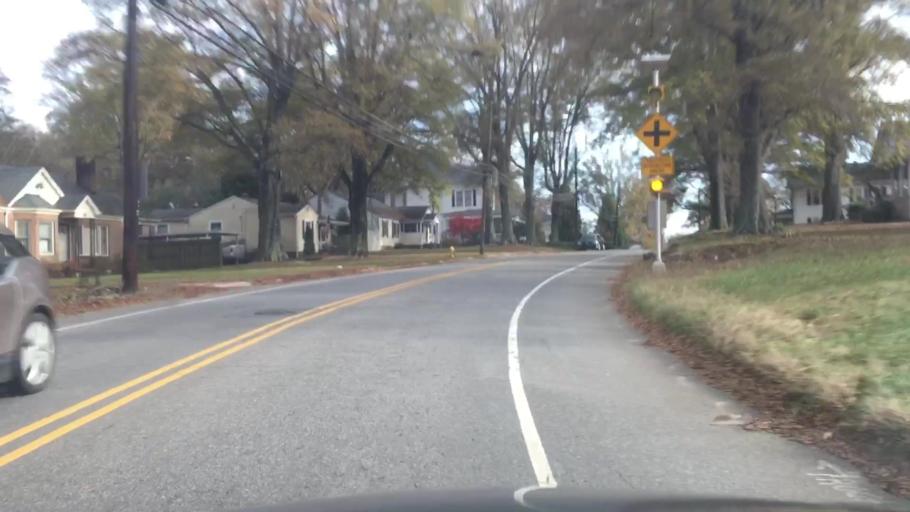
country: US
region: North Carolina
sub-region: Iredell County
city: Mooresville
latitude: 35.5806
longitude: -80.8210
